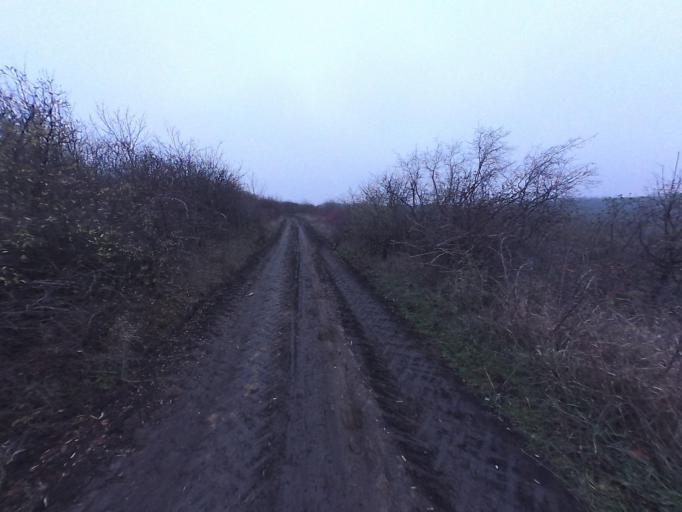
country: RO
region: Galati
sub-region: Comuna Balabanesti
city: Balabanesti
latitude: 46.1452
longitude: 27.7405
